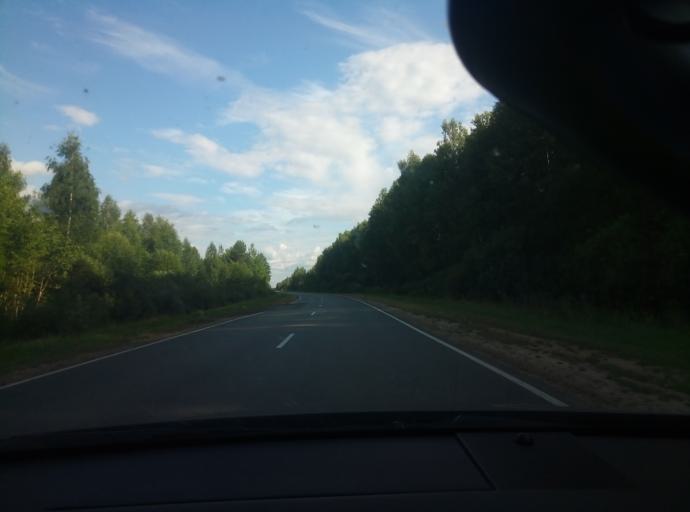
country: RU
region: Kaluga
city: Yukhnov
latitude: 54.6798
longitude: 35.2972
